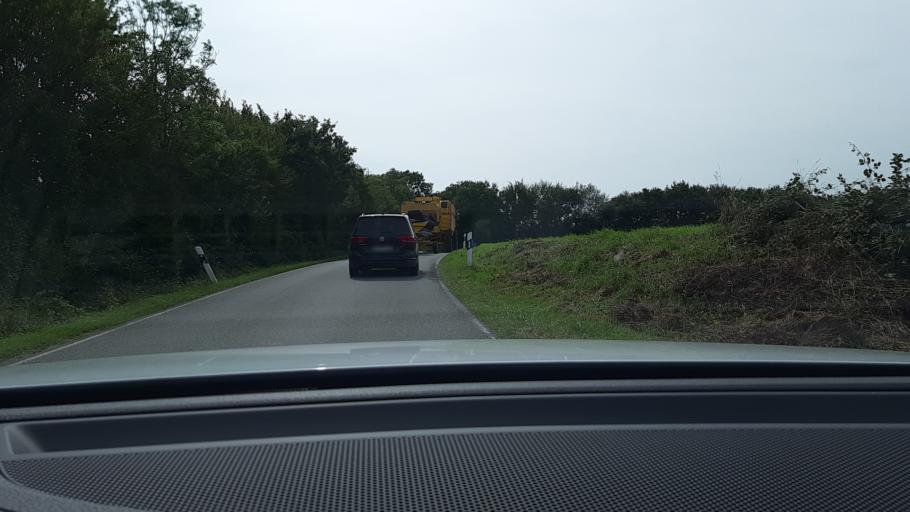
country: DE
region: Schleswig-Holstein
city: Rehhorst
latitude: 53.8650
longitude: 10.4682
